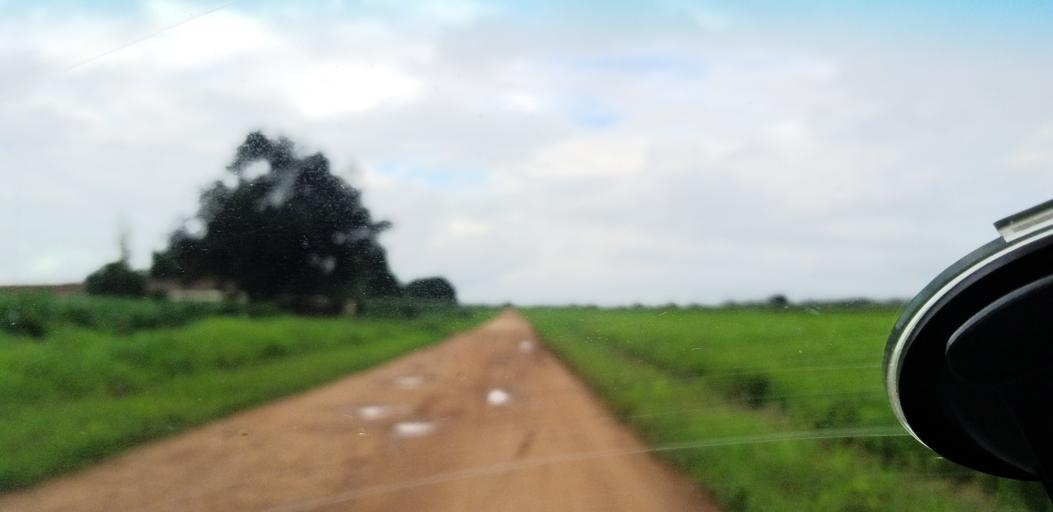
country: ZM
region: Lusaka
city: Lusaka
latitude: -15.5236
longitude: 28.3007
